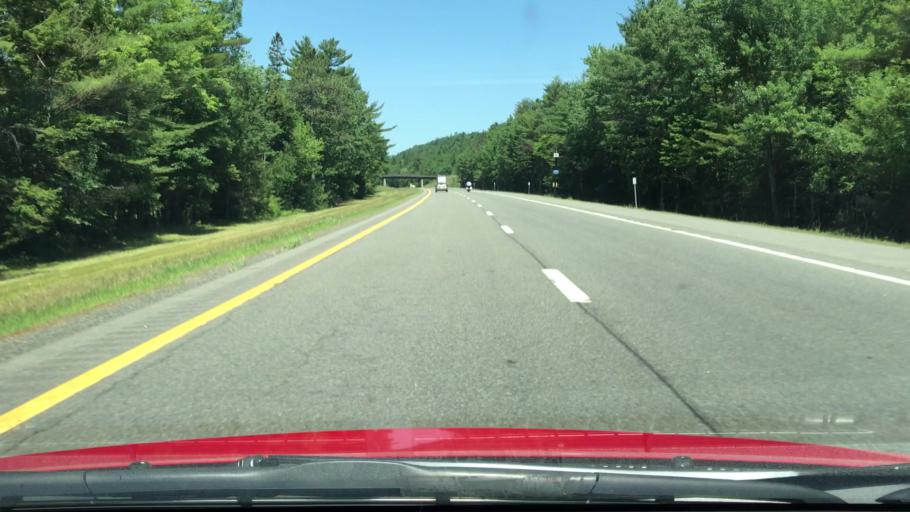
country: US
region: New York
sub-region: Essex County
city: Elizabethtown
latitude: 44.3218
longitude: -73.5283
